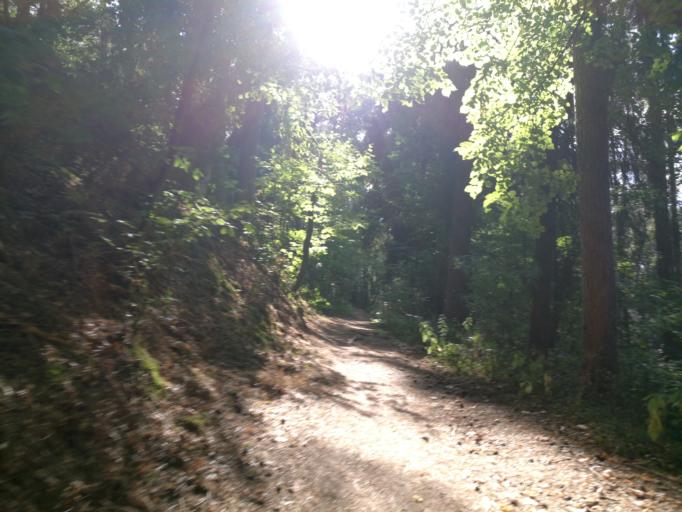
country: DE
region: Bavaria
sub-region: Regierungsbezirk Mittelfranken
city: Seukendorf
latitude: 49.4750
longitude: 10.9155
